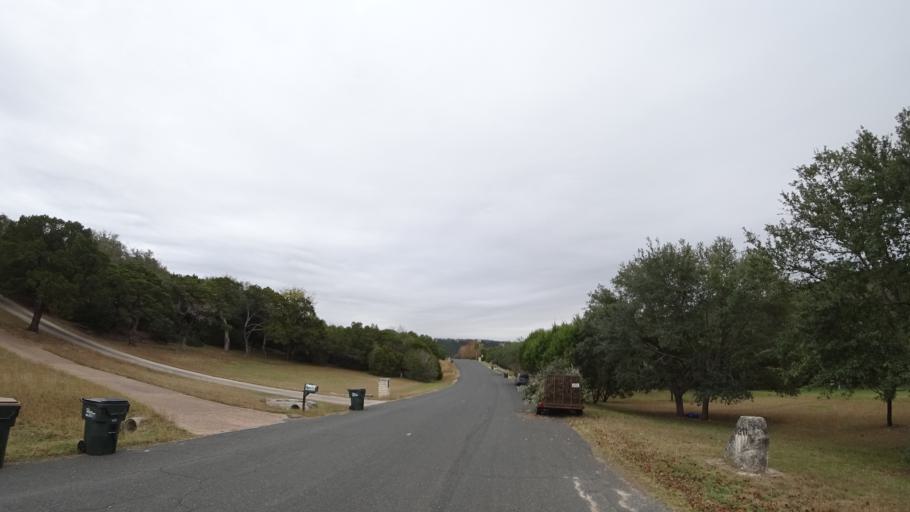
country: US
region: Texas
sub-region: Travis County
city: West Lake Hills
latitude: 30.3714
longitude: -97.8157
